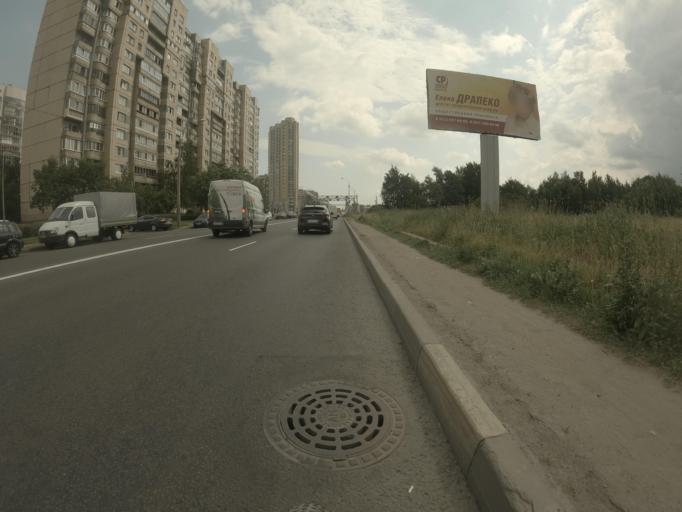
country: RU
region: St.-Petersburg
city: Krasnogvargeisky
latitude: 59.9373
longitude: 30.4726
